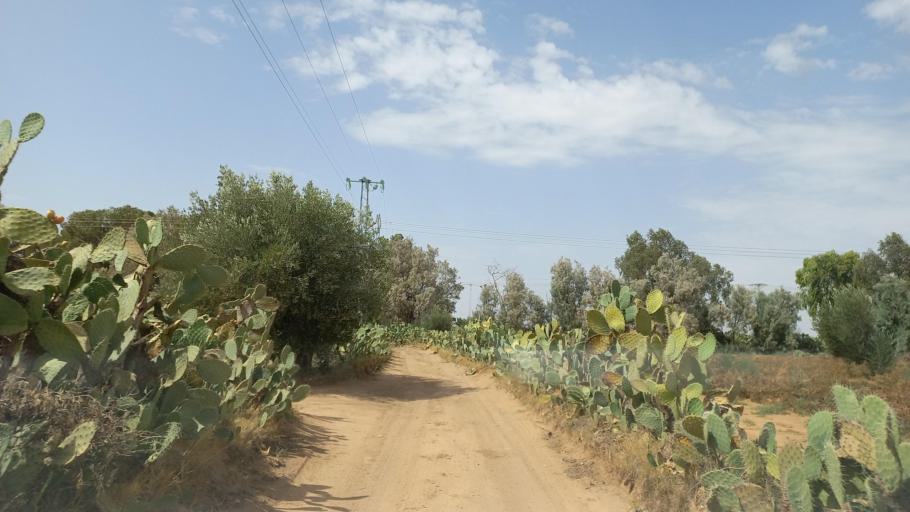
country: TN
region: Al Qasrayn
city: Kasserine
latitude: 35.2626
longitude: 9.0512
